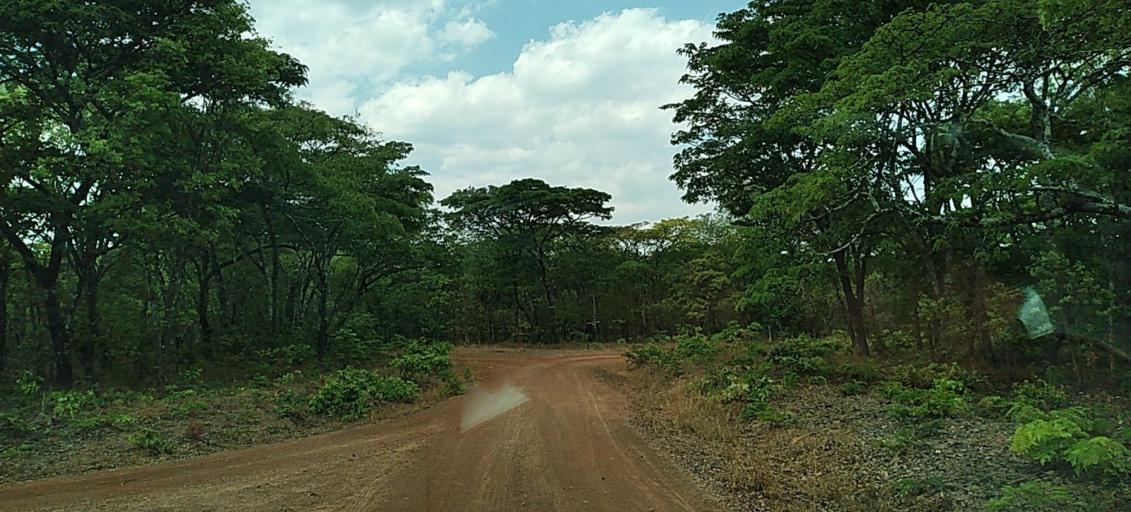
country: ZM
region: Copperbelt
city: Chililabombwe
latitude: -12.4599
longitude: 27.5943
